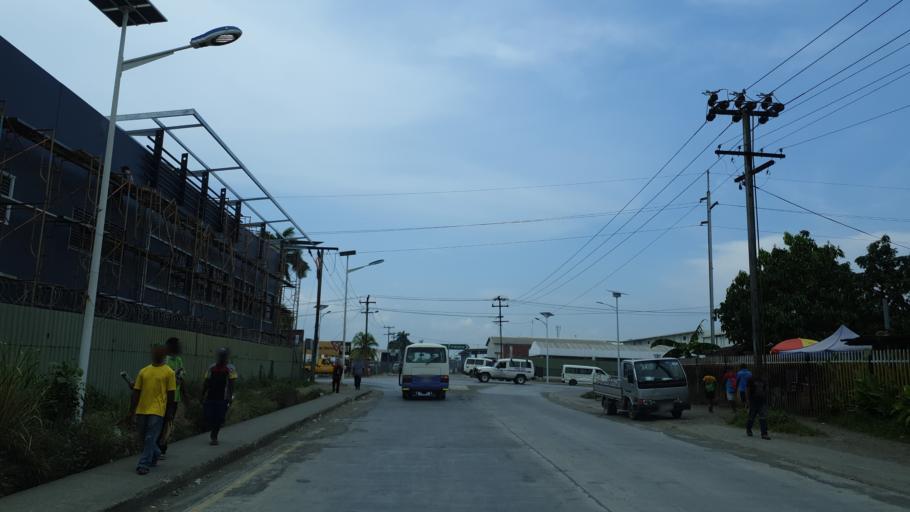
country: PG
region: Morobe
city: Lae
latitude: -6.7310
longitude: 146.9884
